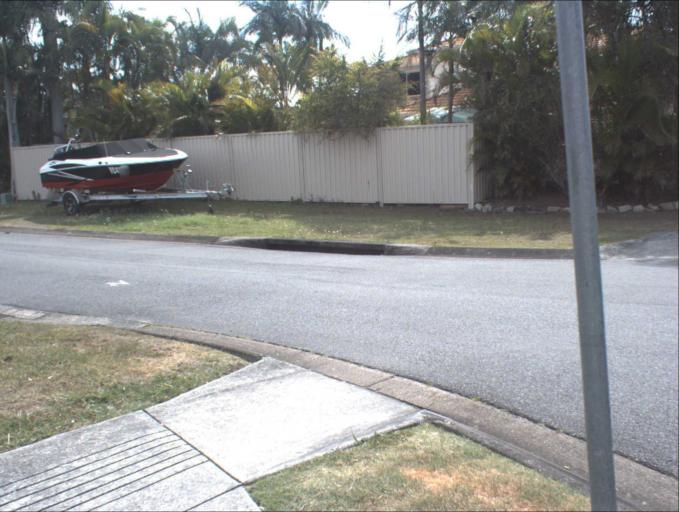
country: AU
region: Queensland
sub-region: Logan
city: Beenleigh
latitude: -27.6773
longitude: 153.2101
